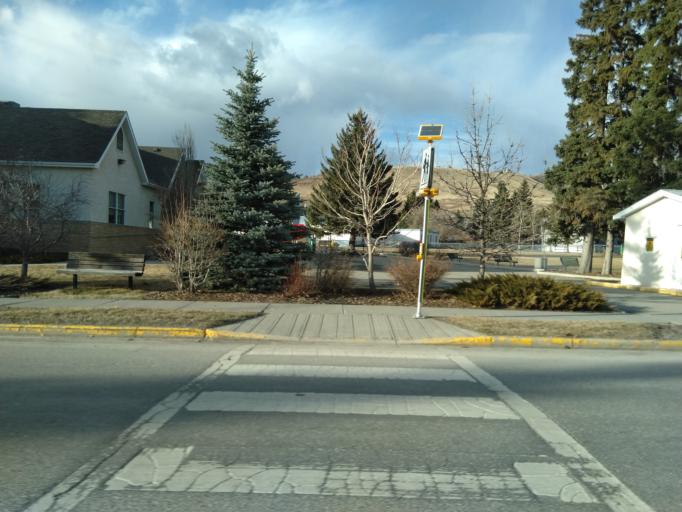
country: CA
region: Alberta
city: Cochrane
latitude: 51.1884
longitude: -114.4648
